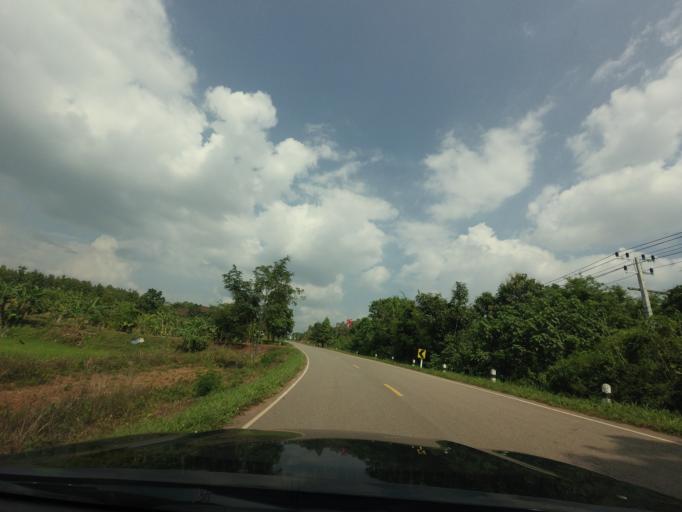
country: TH
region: Uttaradit
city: Ban Khok
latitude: 18.0313
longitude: 101.0858
